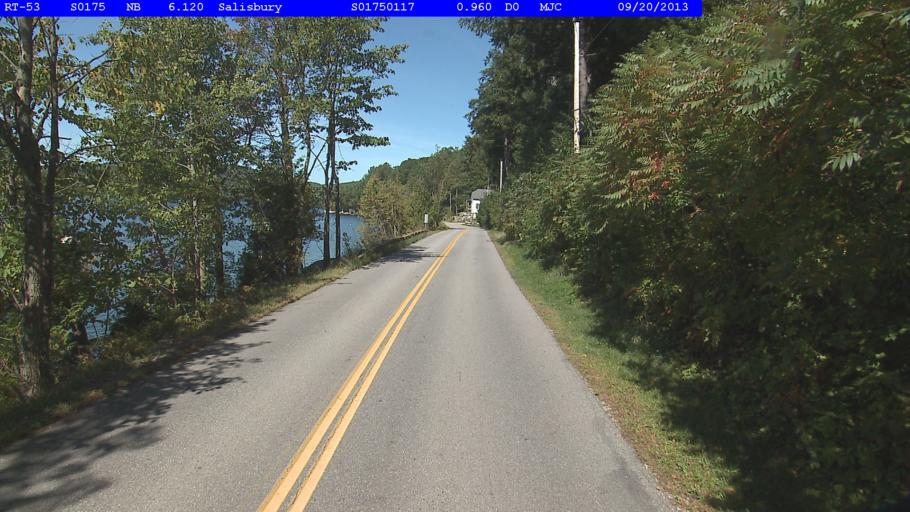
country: US
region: Vermont
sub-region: Rutland County
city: Brandon
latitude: 43.9113
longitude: -73.0669
